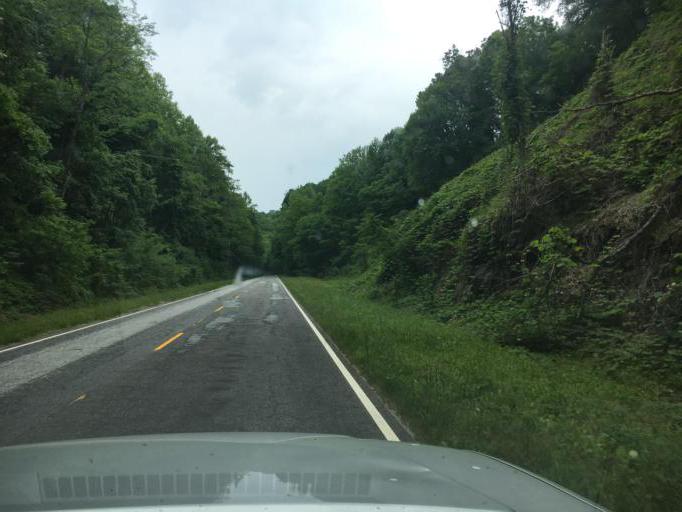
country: US
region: South Carolina
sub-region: Greenville County
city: Tigerville
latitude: 35.1456
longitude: -82.4220
